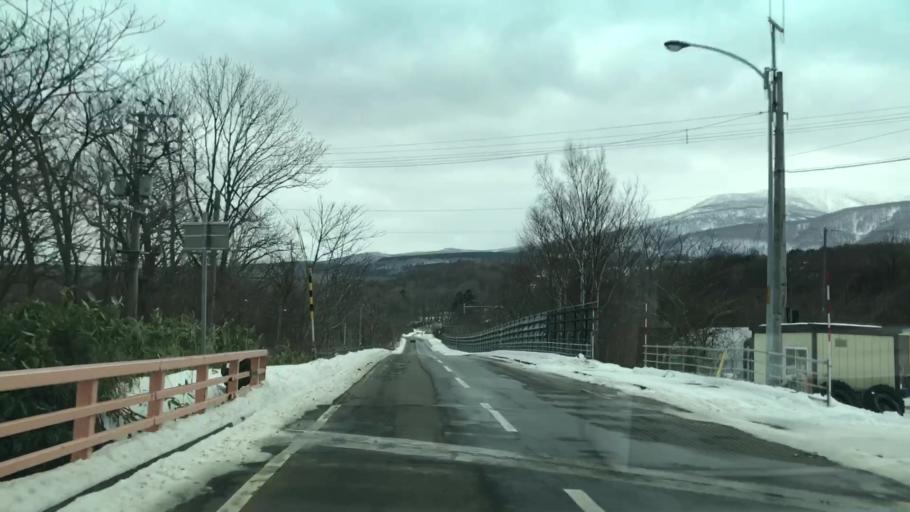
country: JP
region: Hokkaido
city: Yoichi
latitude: 43.3341
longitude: 140.4661
